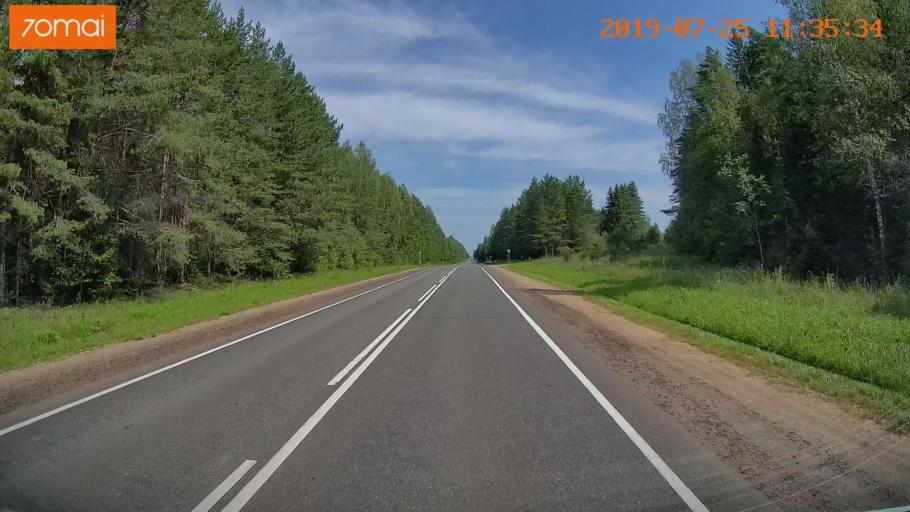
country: RU
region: Ivanovo
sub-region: Privolzhskiy Rayon
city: Ples
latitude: 57.4135
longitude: 41.4314
